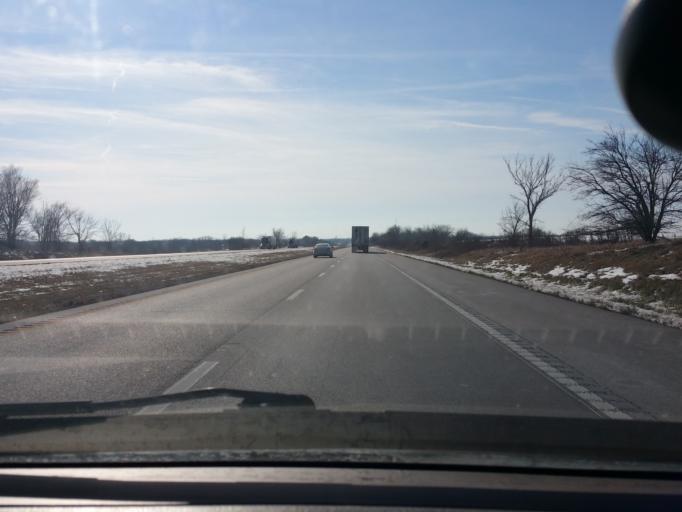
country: US
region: Missouri
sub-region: Clinton County
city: Cameron
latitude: 39.7864
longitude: -94.2067
